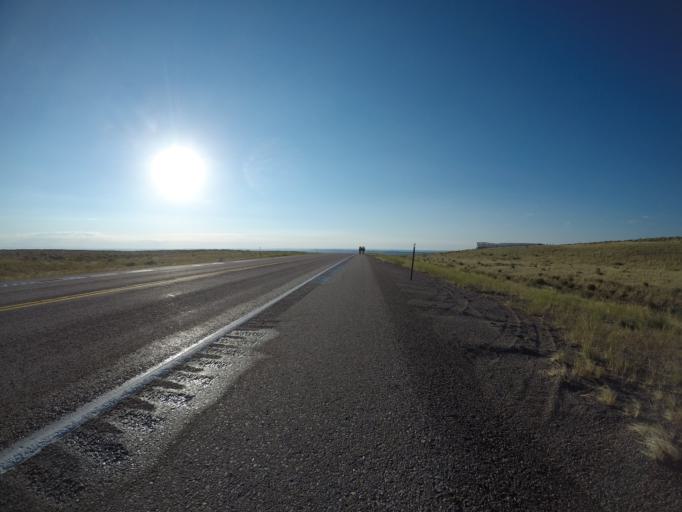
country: US
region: Wyoming
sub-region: Lincoln County
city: Kemmerer
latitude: 41.8895
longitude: -110.3954
